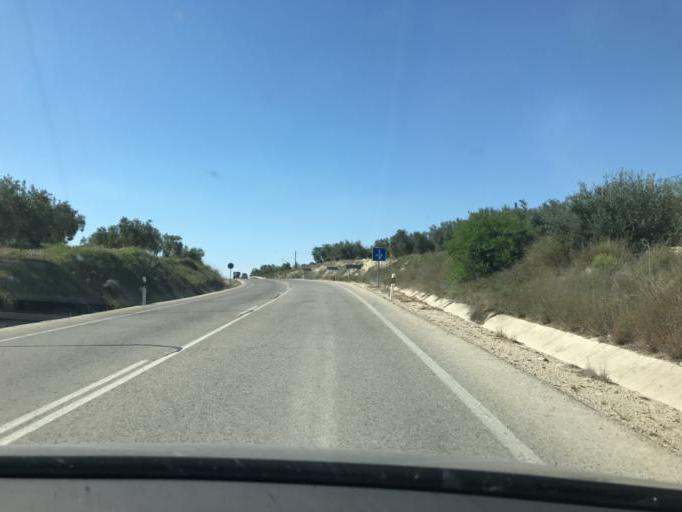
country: ES
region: Andalusia
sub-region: Province of Cordoba
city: Luque
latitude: 37.5903
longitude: -4.2958
